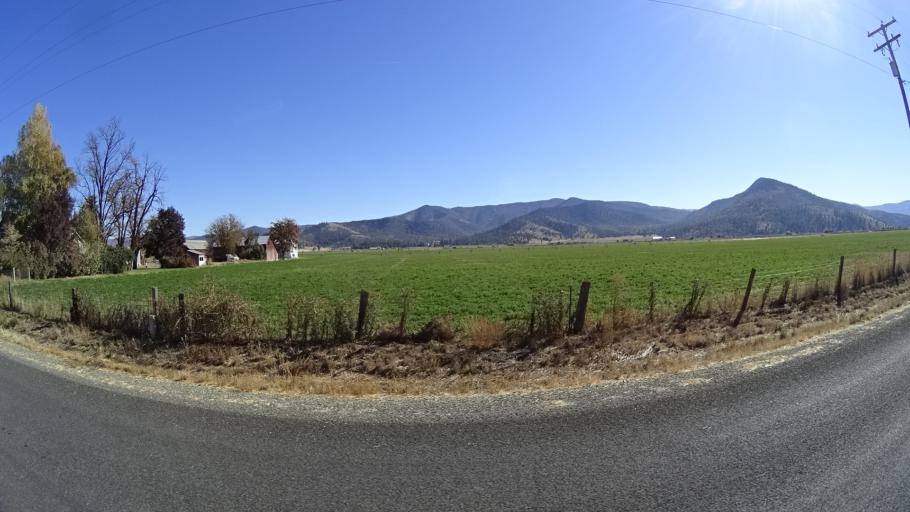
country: US
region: California
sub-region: Siskiyou County
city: Yreka
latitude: 41.5464
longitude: -122.8528
